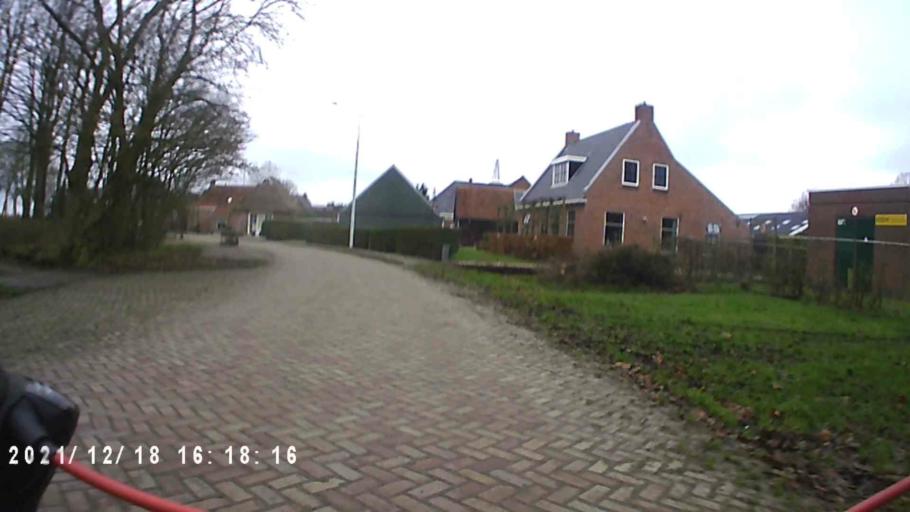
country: NL
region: Friesland
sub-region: Gemeente Dongeradeel
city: Anjum
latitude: 53.3771
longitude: 6.0568
